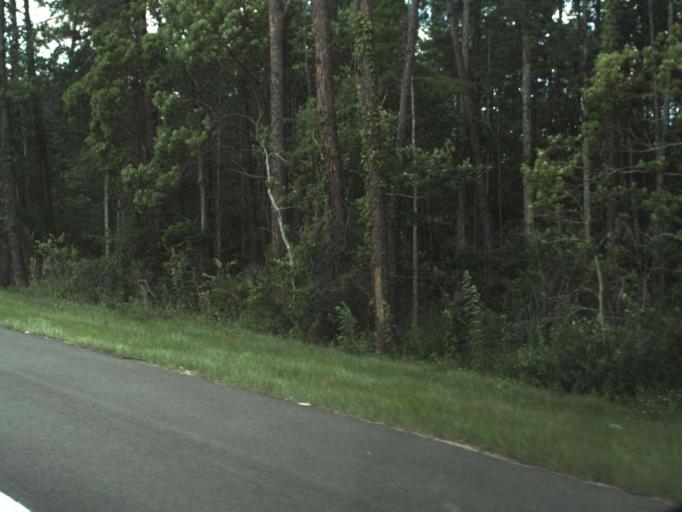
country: US
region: Florida
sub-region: Volusia County
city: Lake Helen
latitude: 29.0461
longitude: -81.2051
